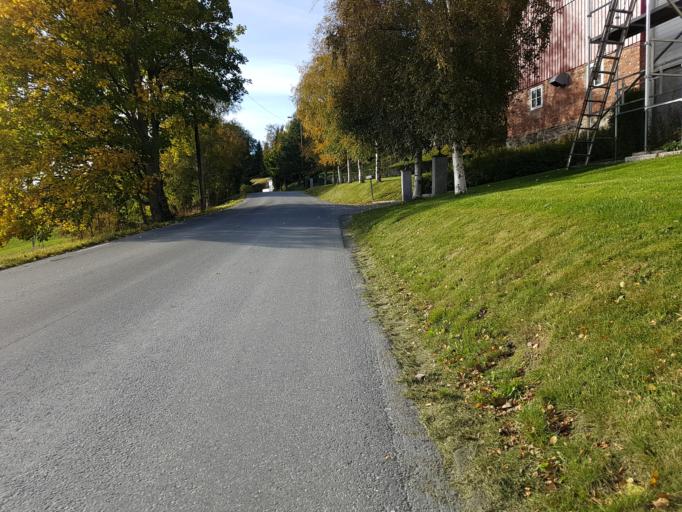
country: NO
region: Sor-Trondelag
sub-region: Klaebu
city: Klaebu
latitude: 63.3499
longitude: 10.4947
